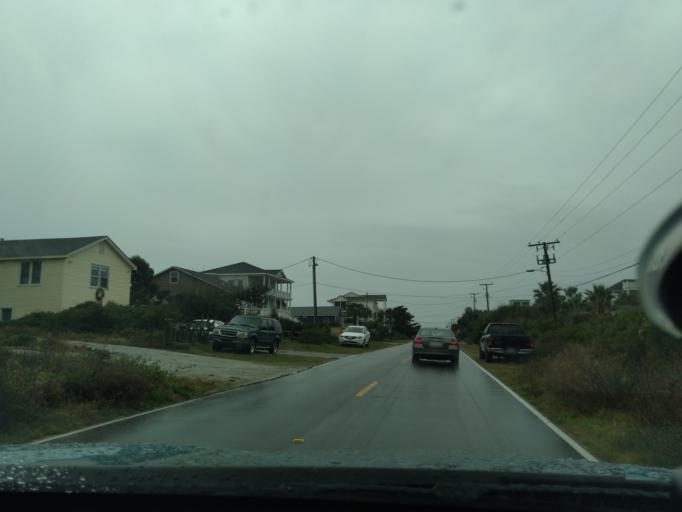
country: US
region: South Carolina
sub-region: Charleston County
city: Folly Beach
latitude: 32.6730
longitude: -79.9032
